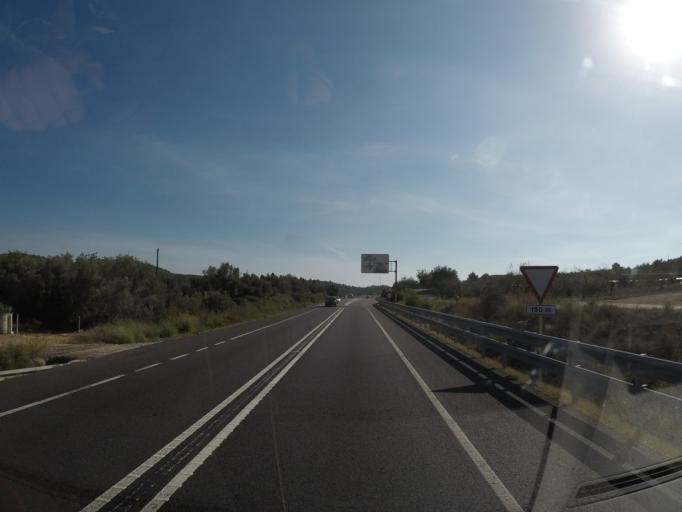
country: ES
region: Catalonia
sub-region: Provincia de Tarragona
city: El Perello
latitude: 40.8841
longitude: 0.7187
